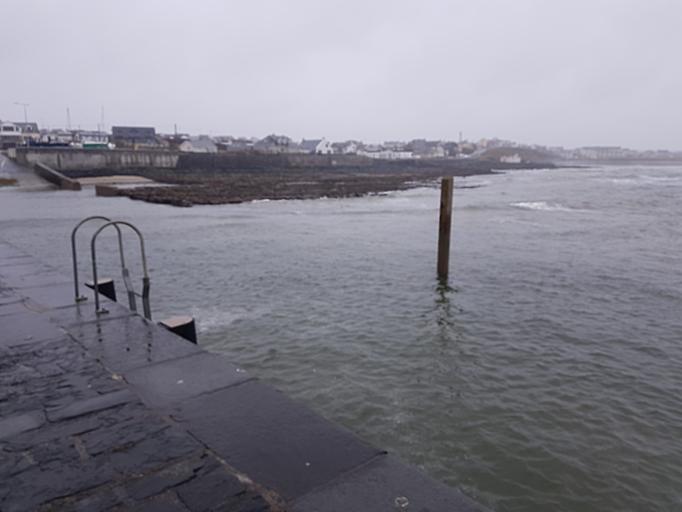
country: IE
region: Connaught
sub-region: Sligo
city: Inishcrone
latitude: 54.2202
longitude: -9.0980
